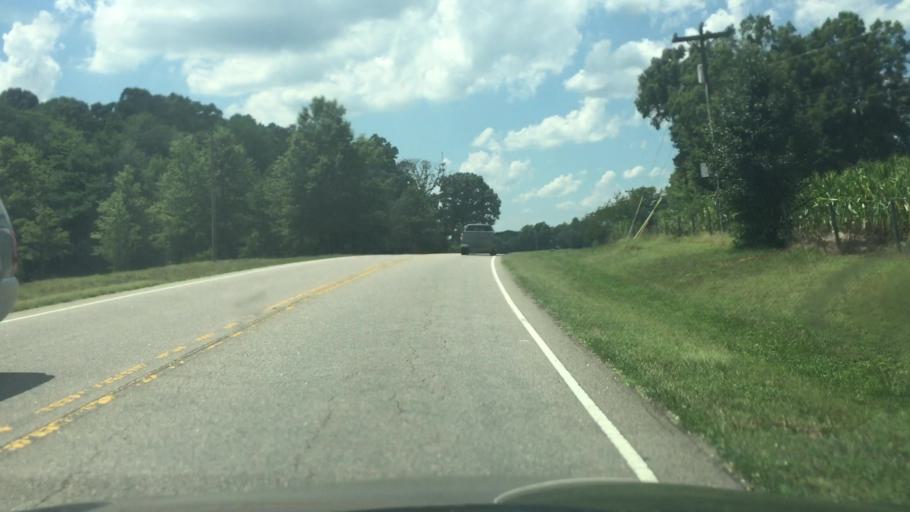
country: US
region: North Carolina
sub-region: Rowan County
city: Enochville
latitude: 35.5728
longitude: -80.6855
